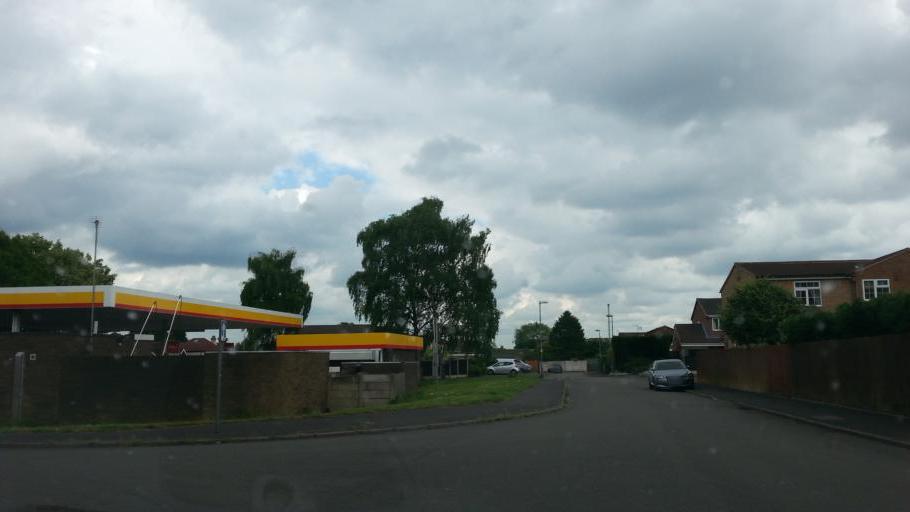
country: GB
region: England
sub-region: Sandwell
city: Tipton
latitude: 52.5326
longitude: -2.0941
